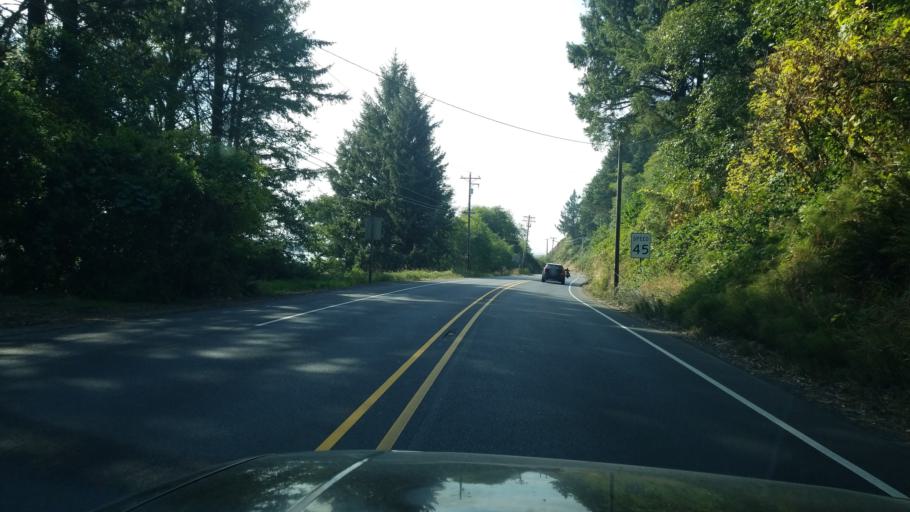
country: US
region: Oregon
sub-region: Tillamook County
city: Bay City
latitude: 45.5594
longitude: -123.9283
